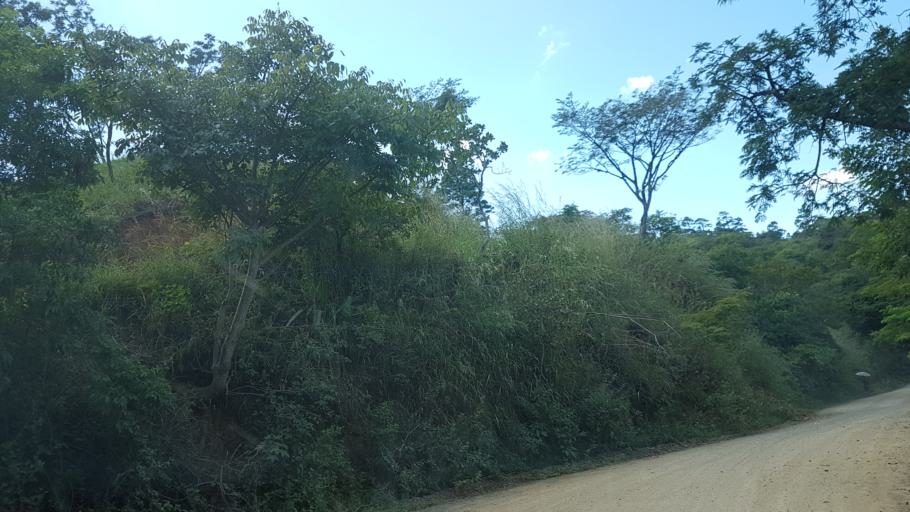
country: HN
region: El Paraiso
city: Oropoli
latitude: 13.7417
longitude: -86.7048
